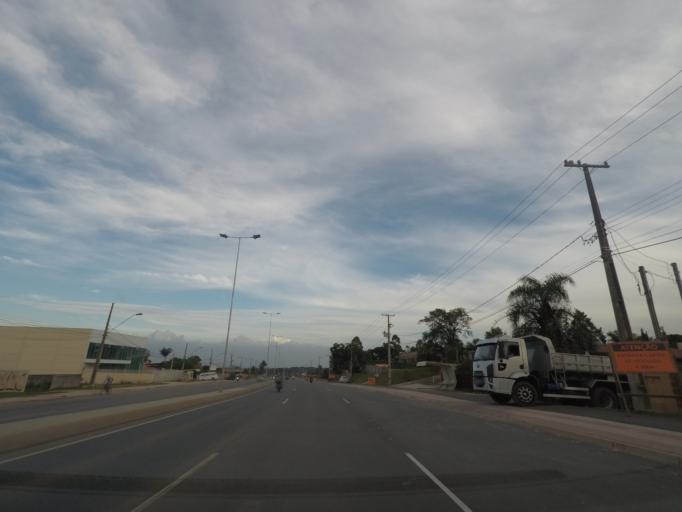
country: BR
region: Parana
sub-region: Colombo
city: Colombo
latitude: -25.3051
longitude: -49.2232
